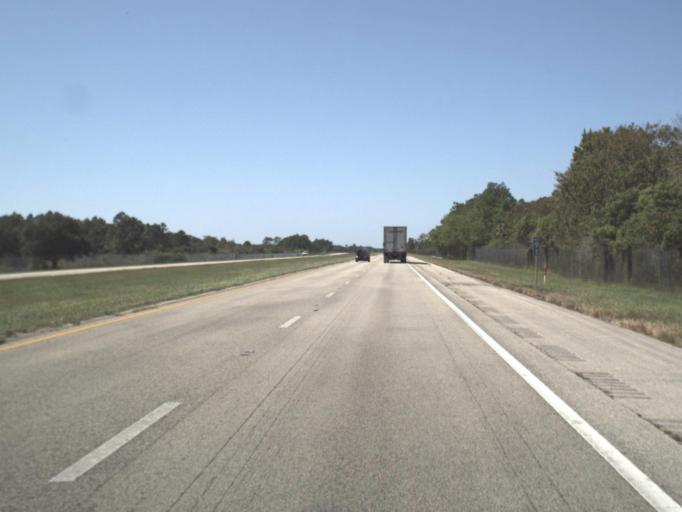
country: US
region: Florida
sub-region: Collier County
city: Orangetree
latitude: 26.1533
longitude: -81.5158
